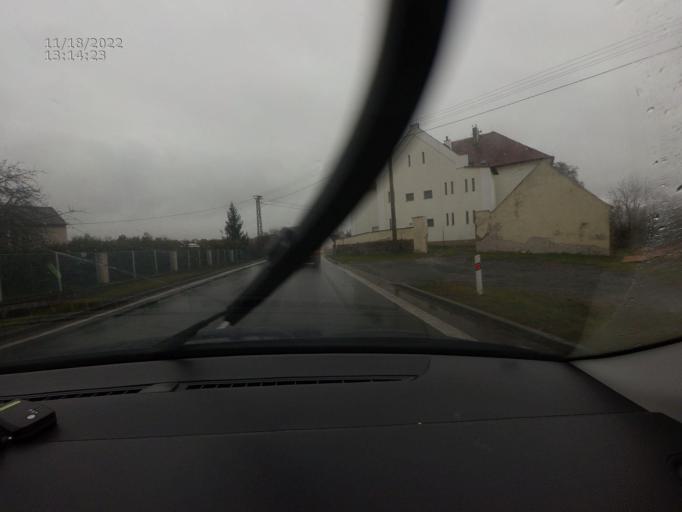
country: CZ
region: Plzensky
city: Horazd'ovice
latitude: 49.3286
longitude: 13.6454
